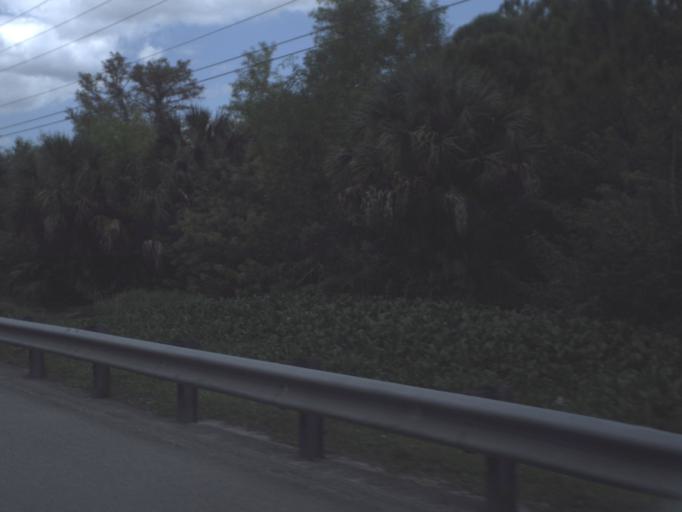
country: US
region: Florida
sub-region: Collier County
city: Lely Resort
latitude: 26.0226
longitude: -81.6354
